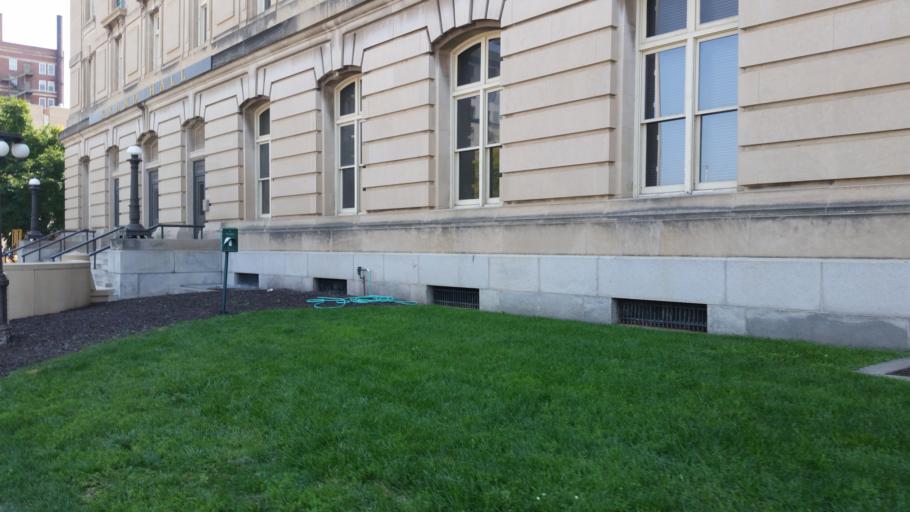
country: US
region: Nebraska
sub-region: Lancaster County
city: Lincoln
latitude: 40.8146
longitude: -96.7077
